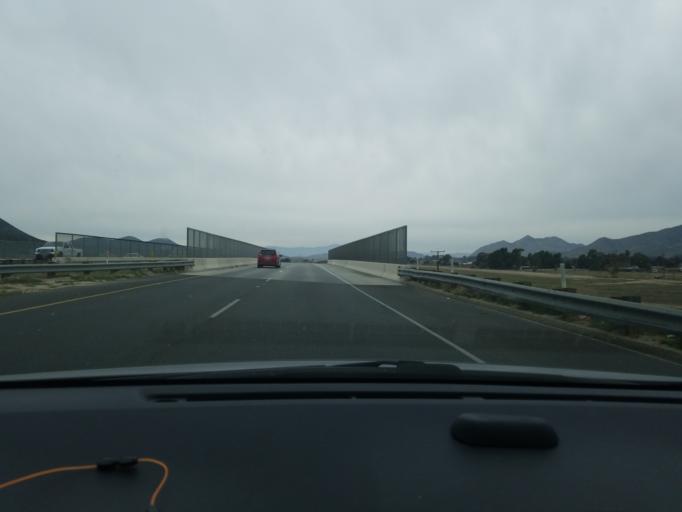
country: US
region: California
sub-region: Riverside County
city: Winchester
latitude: 33.6987
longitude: -117.0469
